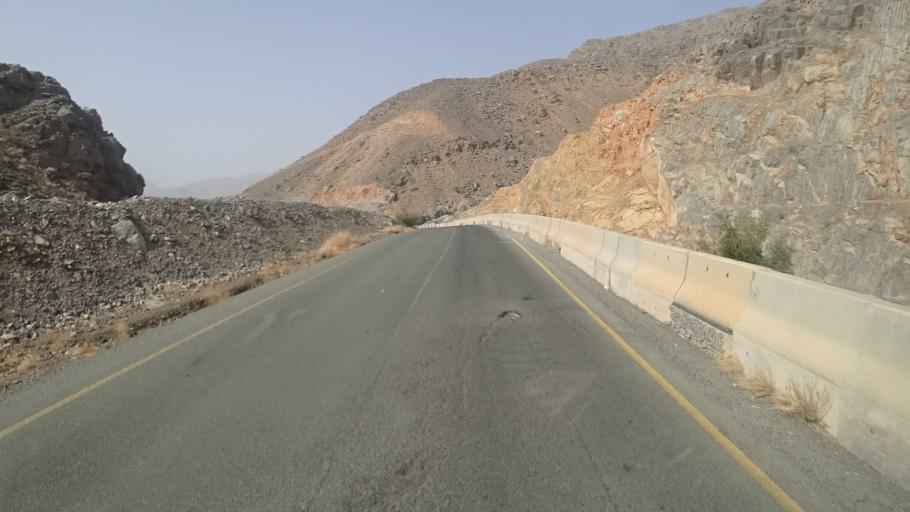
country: OM
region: Muhafazat ad Dakhiliyah
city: Nizwa
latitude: 22.9582
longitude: 57.5936
